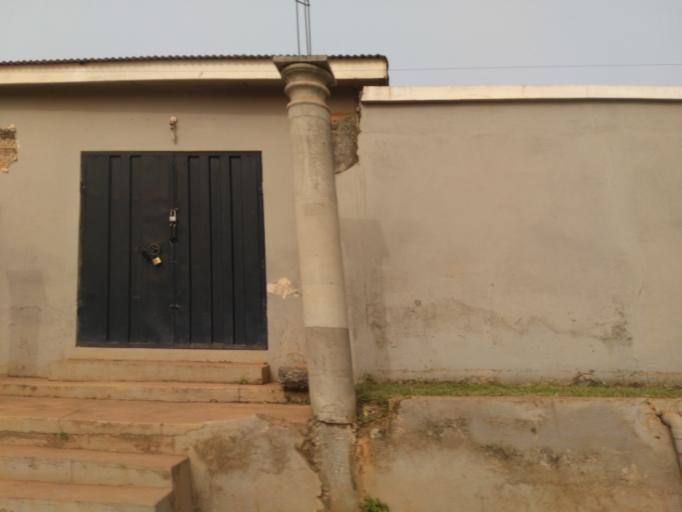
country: GH
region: Ashanti
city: Kumasi
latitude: 6.6417
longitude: -1.6252
